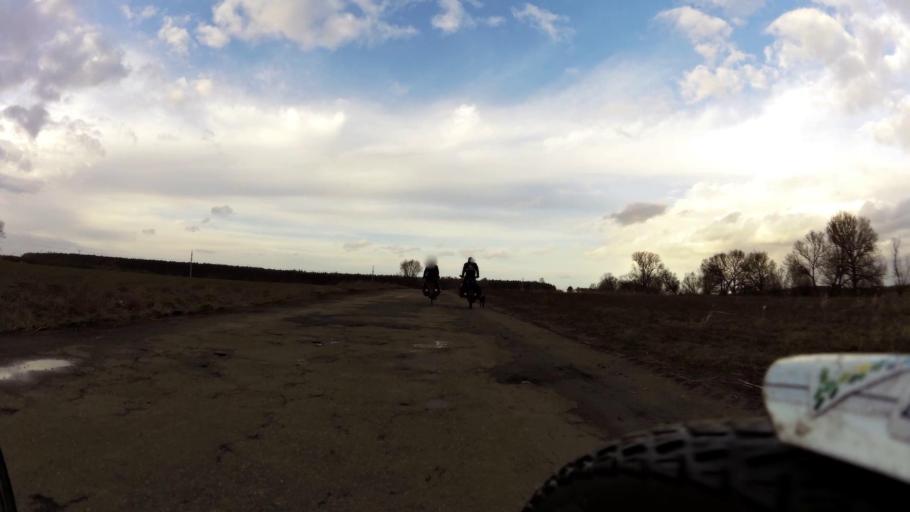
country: PL
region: West Pomeranian Voivodeship
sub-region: Powiat kamienski
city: Kamien Pomorski
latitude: 53.9004
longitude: 14.7318
